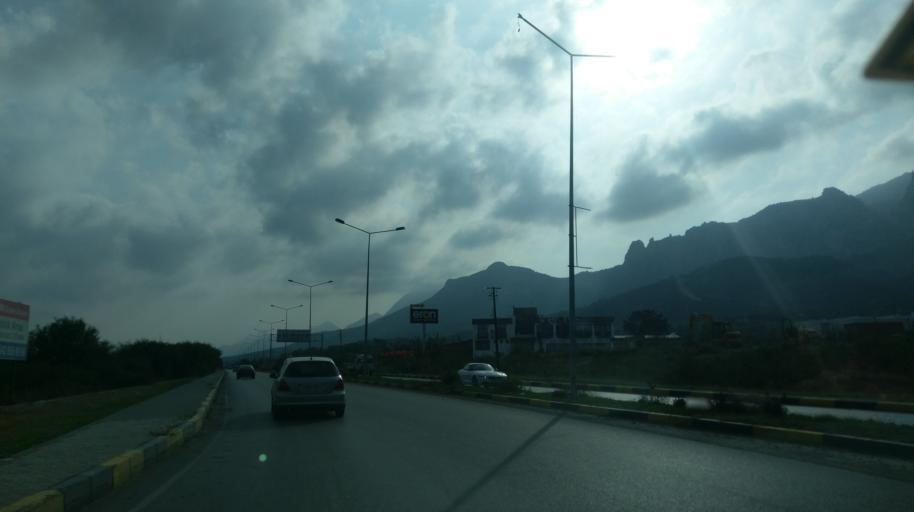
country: CY
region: Keryneia
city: Kyrenia
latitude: 35.3311
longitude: 33.2754
